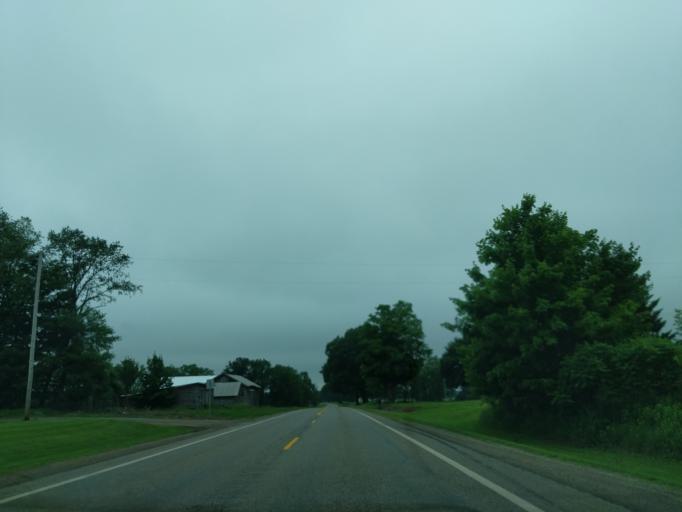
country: US
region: Michigan
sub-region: Hillsdale County
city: Litchfield
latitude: 42.0838
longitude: -84.8029
